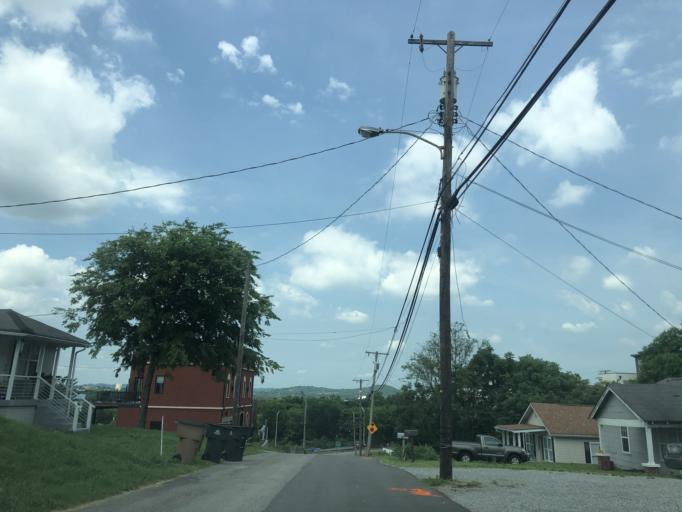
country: US
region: Tennessee
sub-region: Davidson County
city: Nashville
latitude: 36.1946
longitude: -86.7738
